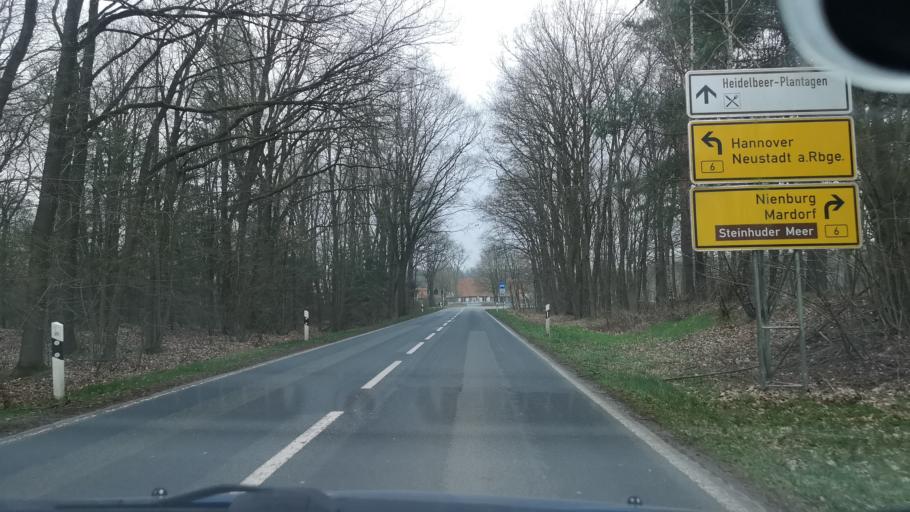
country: DE
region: Lower Saxony
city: Neustadt am Rubenberge
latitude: 52.5382
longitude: 9.4008
